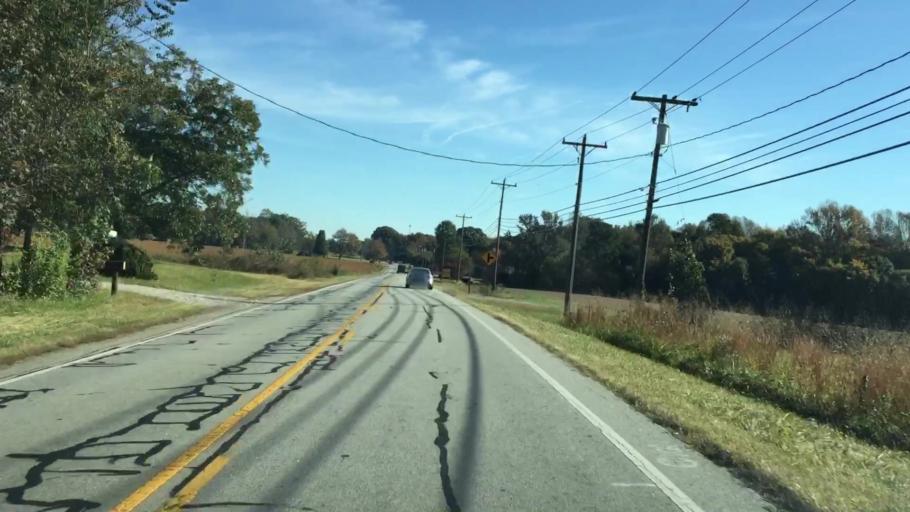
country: US
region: North Carolina
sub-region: Rowan County
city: China Grove
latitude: 35.6537
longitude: -80.5711
